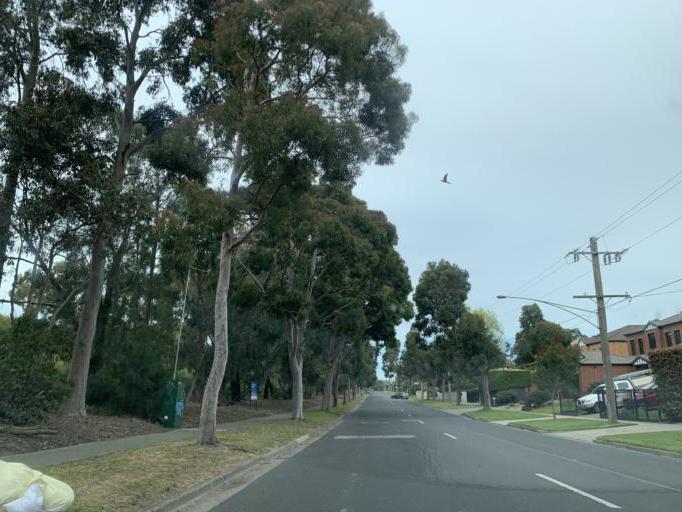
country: AU
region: Victoria
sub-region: Bayside
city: Highett
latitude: -37.9586
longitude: 145.0291
